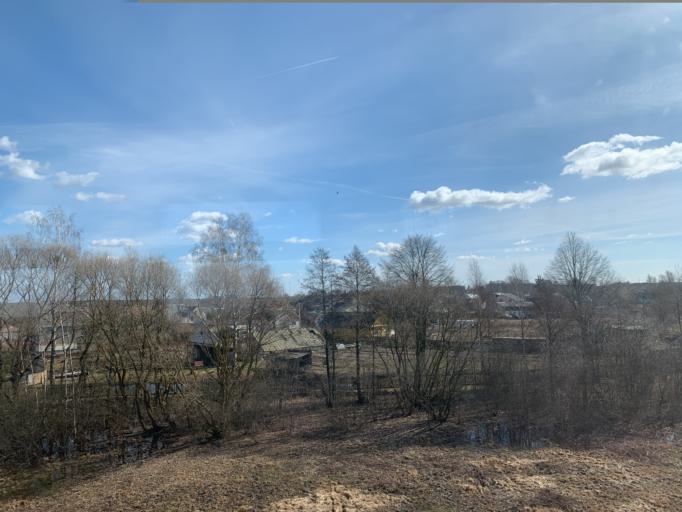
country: BY
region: Minsk
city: Novy Svyerzhan'
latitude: 53.4632
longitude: 26.7248
